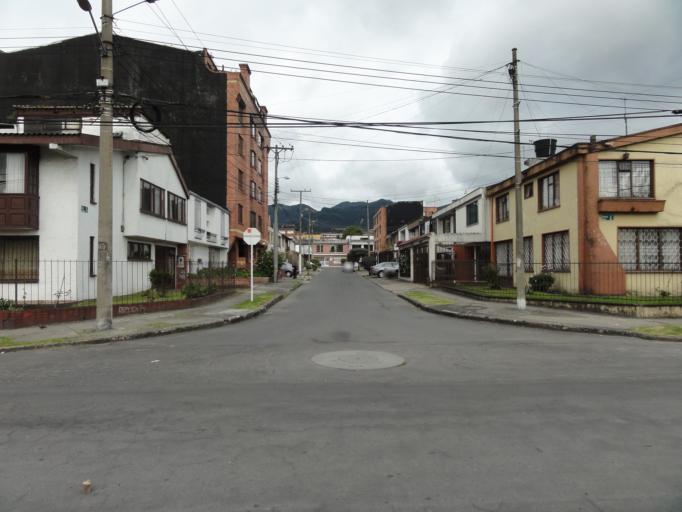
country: CO
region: Bogota D.C.
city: Bogota
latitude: 4.6487
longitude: -74.0811
